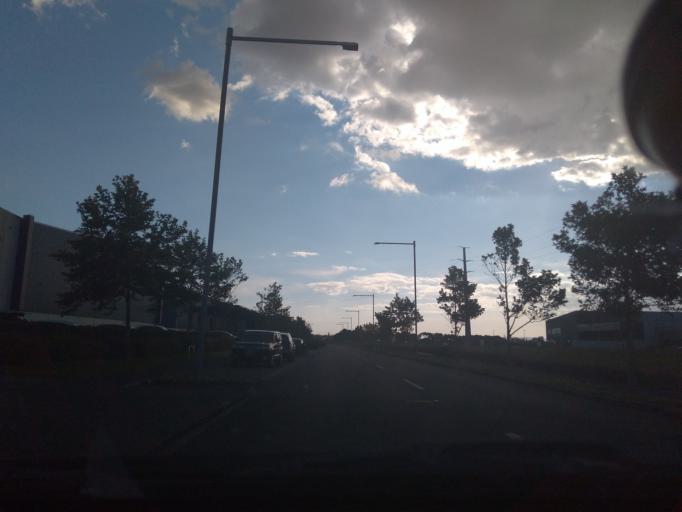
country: NZ
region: Auckland
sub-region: Auckland
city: Tamaki
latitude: -36.9301
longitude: 174.8737
